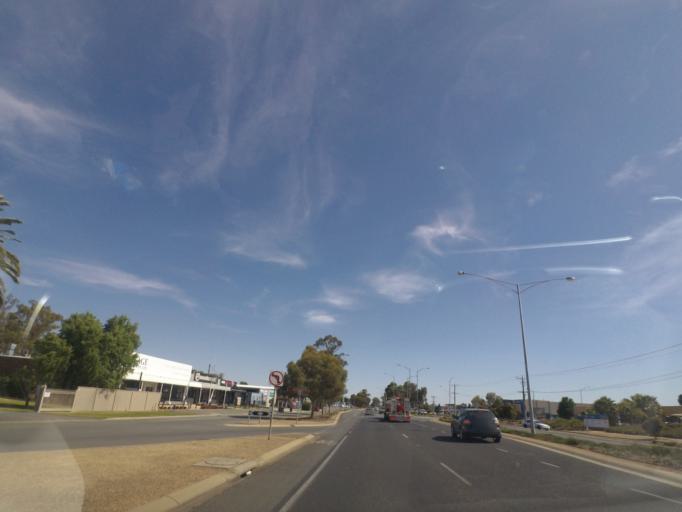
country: AU
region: Victoria
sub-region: Greater Shepparton
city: Shepparton
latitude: -36.4079
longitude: 145.3937
